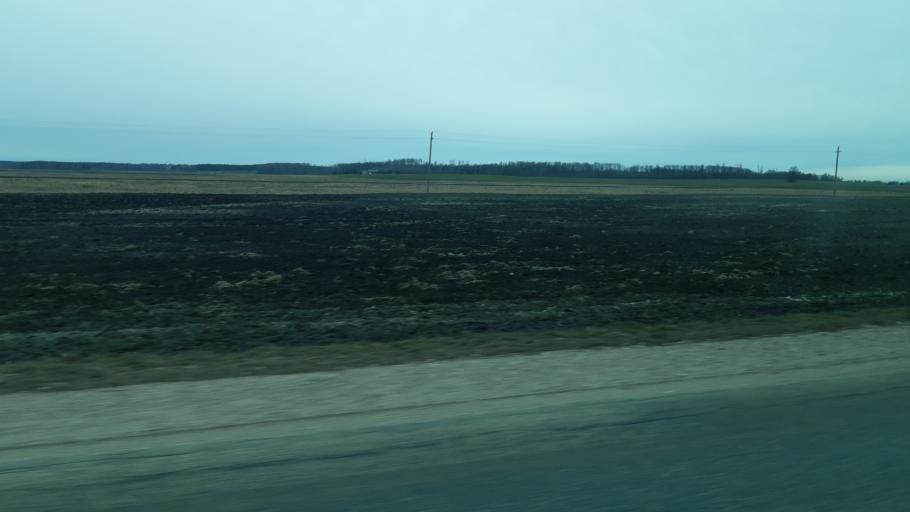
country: LT
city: Kalvarija
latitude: 54.4113
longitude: 23.1822
